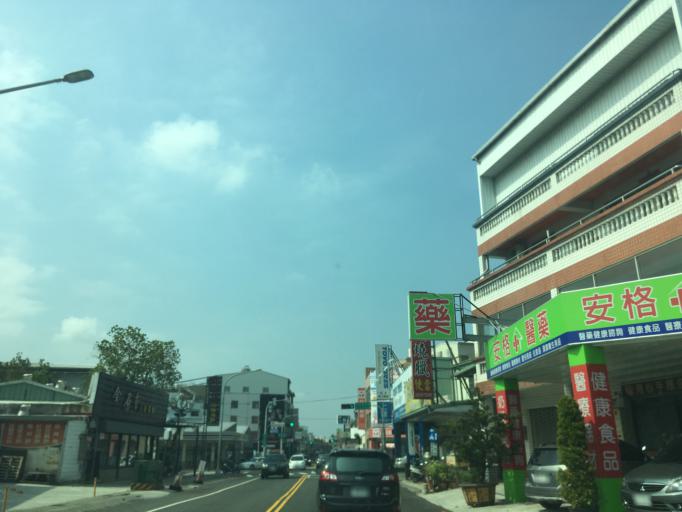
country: TW
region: Taiwan
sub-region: Taichung City
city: Taichung
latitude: 24.1434
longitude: 120.7089
